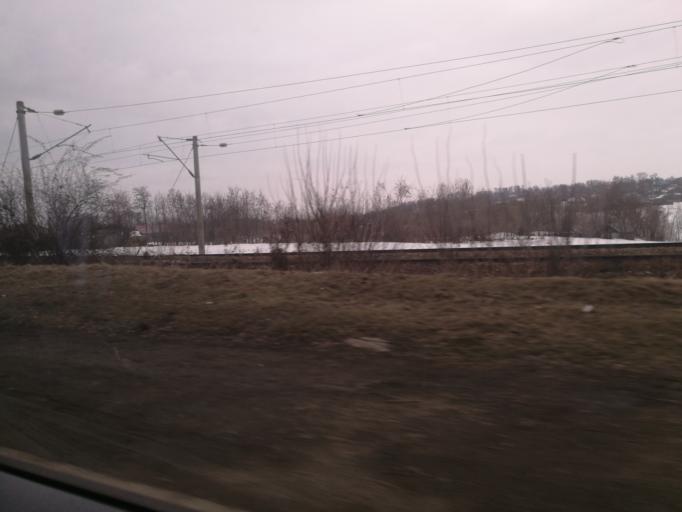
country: RO
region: Iasi
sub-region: Comuna Ruginoasa
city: Rediu
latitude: 47.2472
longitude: 26.8585
